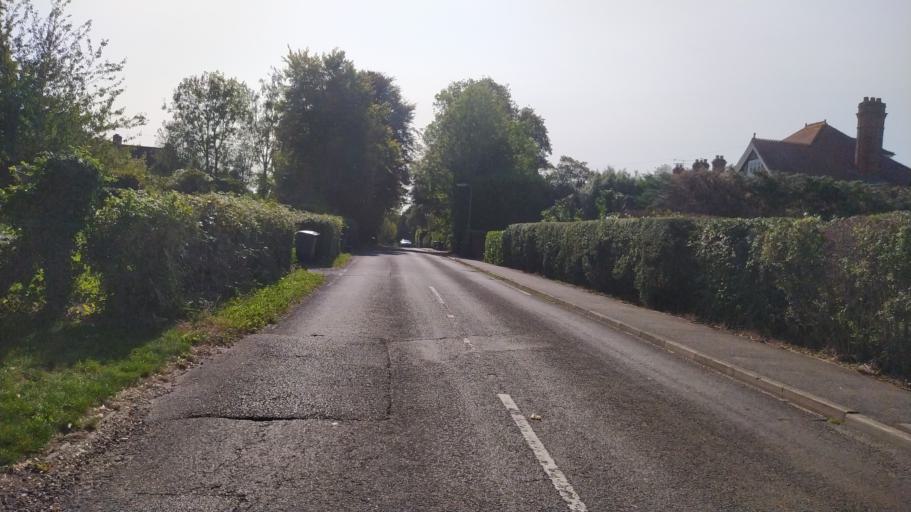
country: GB
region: England
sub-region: Hampshire
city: Havant
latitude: 50.8944
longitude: -0.9614
